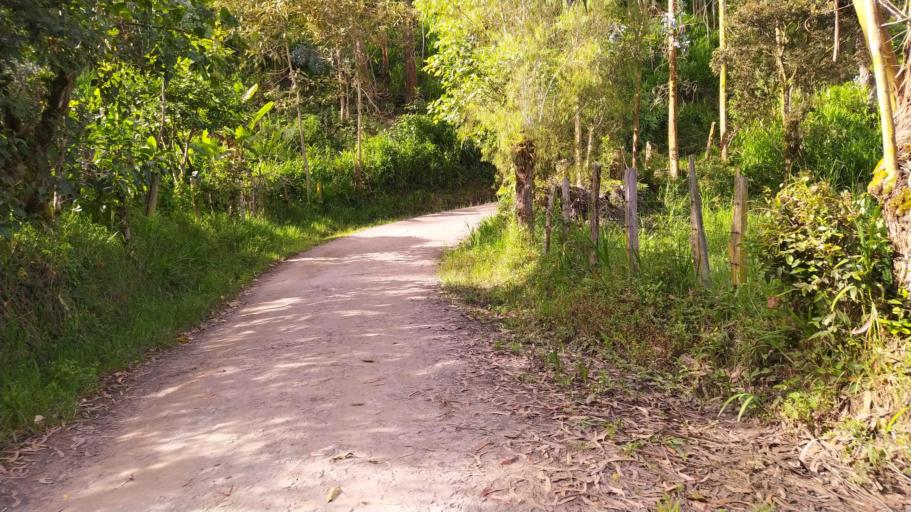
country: CO
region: Cundinamarca
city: Tenza
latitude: 5.0906
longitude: -73.4654
